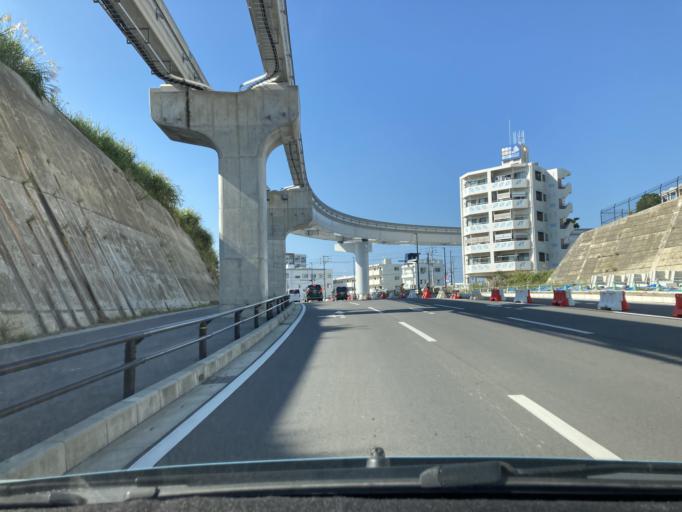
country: JP
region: Okinawa
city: Ginowan
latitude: 26.2351
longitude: 127.7279
